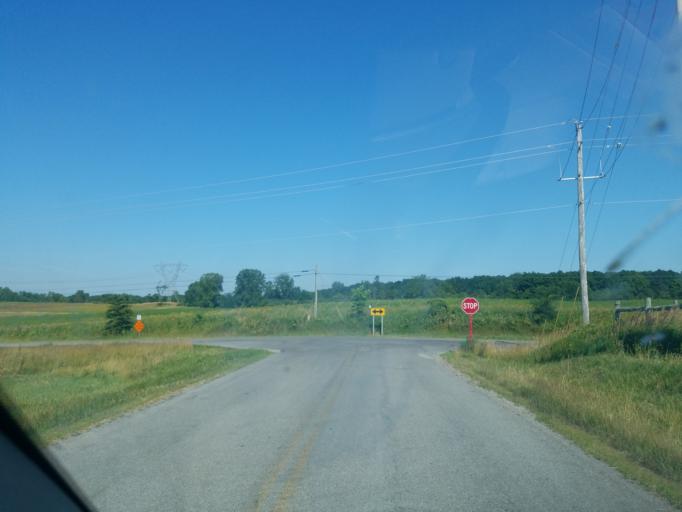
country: US
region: Ohio
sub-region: Logan County
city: Northwood
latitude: 40.4426
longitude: -83.6879
